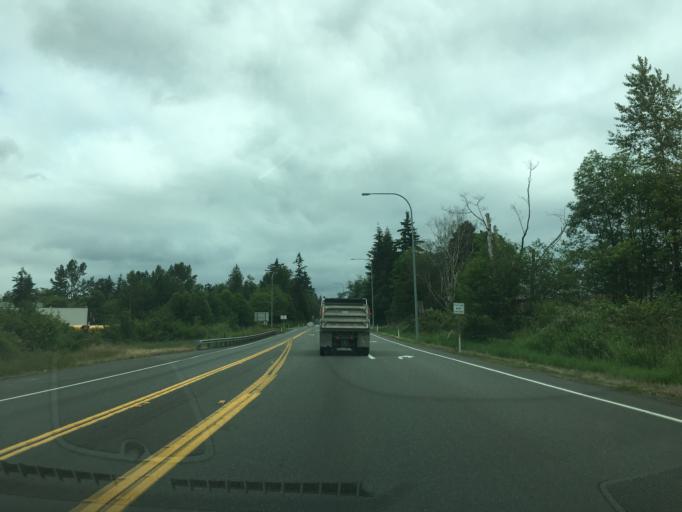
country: US
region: Washington
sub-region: Snohomish County
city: West Lake Stevens
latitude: 48.0326
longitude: -122.1104
